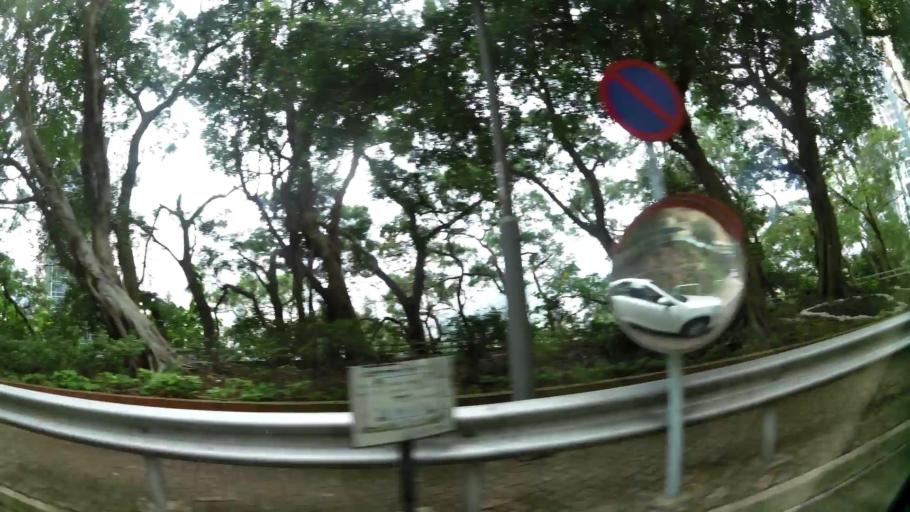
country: HK
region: Central and Western
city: Central
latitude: 22.2432
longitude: 114.1571
